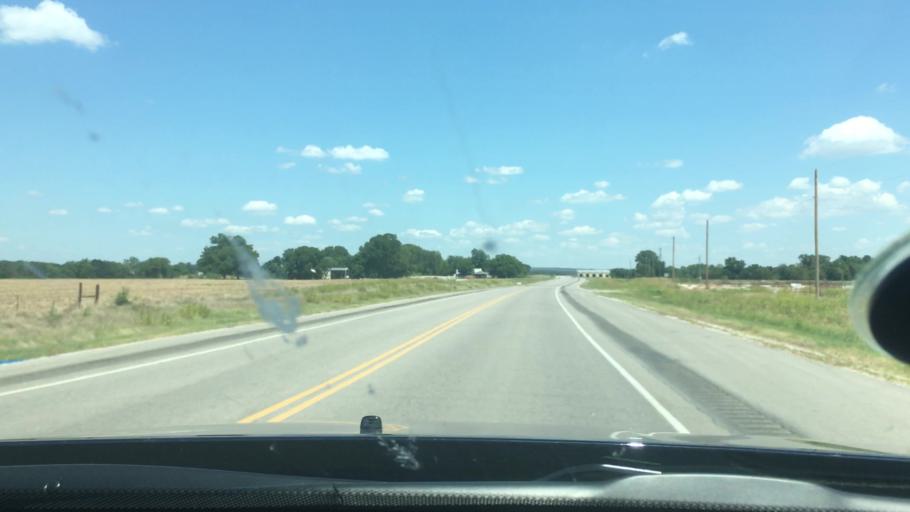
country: US
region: Oklahoma
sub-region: Carter County
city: Dickson
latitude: 34.2278
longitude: -96.9769
